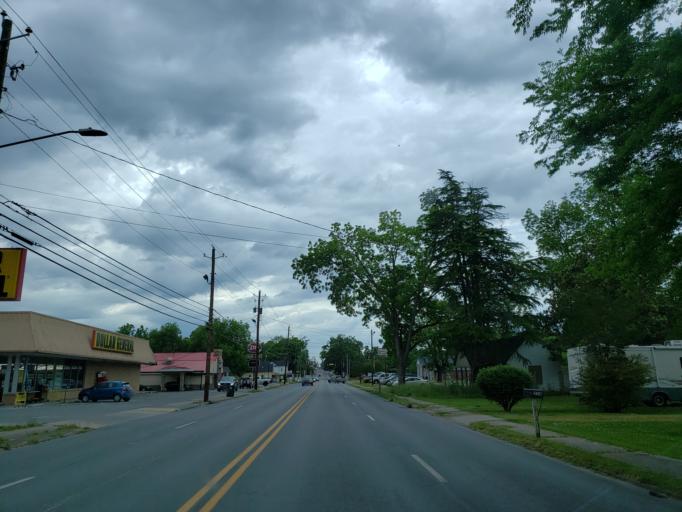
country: US
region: Georgia
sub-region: Polk County
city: Rockmart
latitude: 33.9945
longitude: -85.0415
